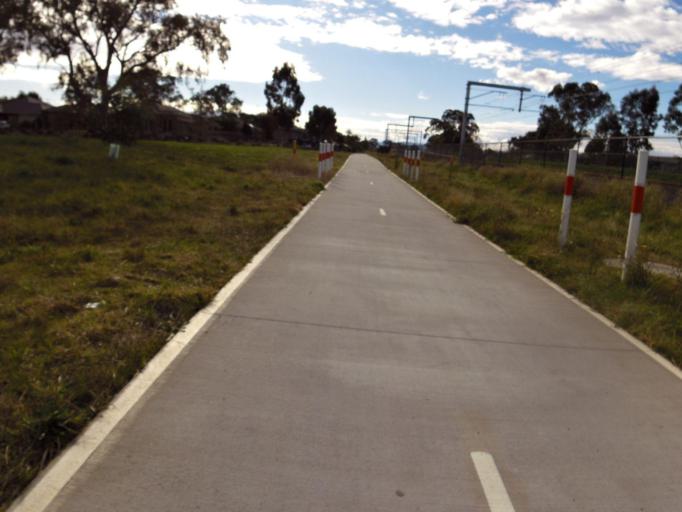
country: AU
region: Victoria
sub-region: Whittlesea
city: Mernda
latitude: -37.6184
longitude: 145.0975
